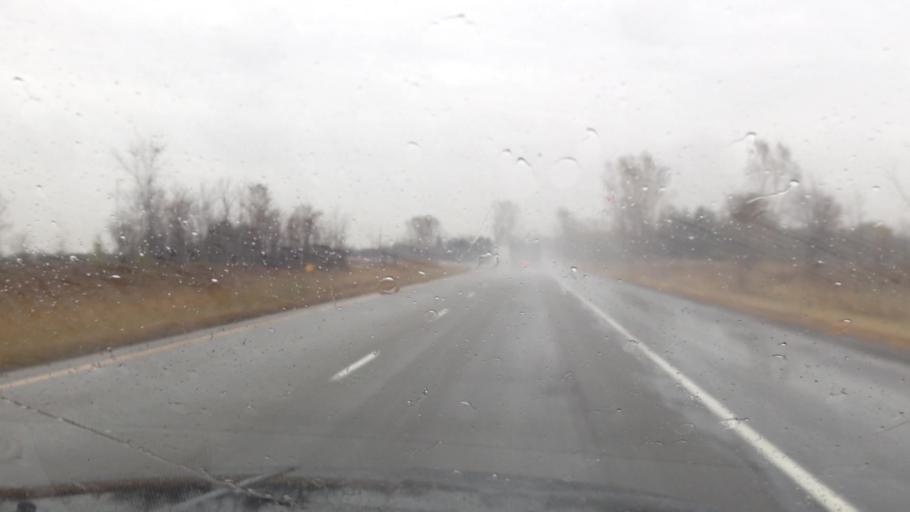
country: CA
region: Ontario
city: Casselman
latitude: 45.3029
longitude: -75.0978
